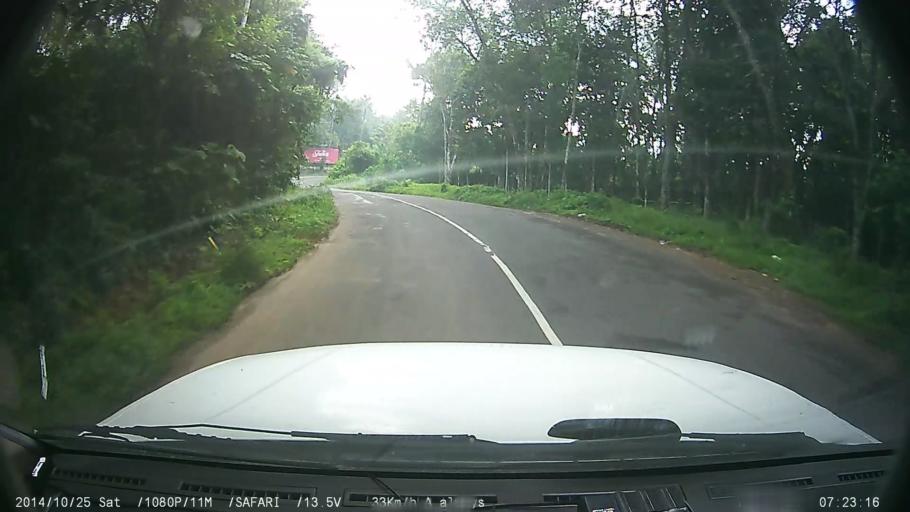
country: IN
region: Kerala
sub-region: Kottayam
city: Palackattumala
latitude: 9.7921
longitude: 76.5765
